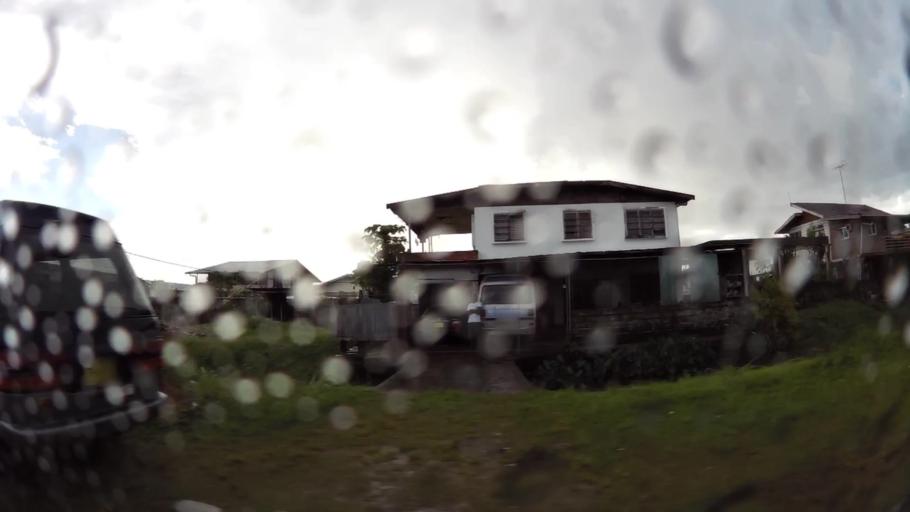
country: SR
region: Paramaribo
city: Paramaribo
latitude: 5.8196
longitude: -55.1863
